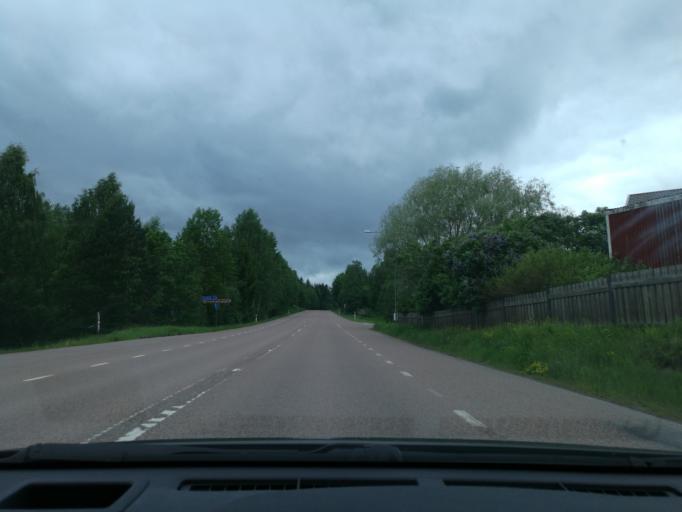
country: SE
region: Dalarna
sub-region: Smedjebackens Kommun
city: Smedjebacken
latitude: 60.1393
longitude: 15.3112
